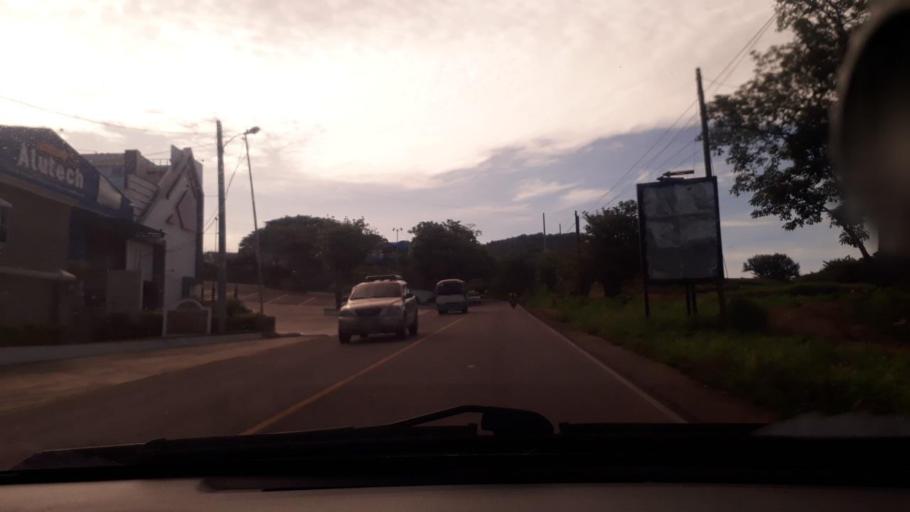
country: GT
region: Jutiapa
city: Jutiapa
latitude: 14.3009
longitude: -89.8871
